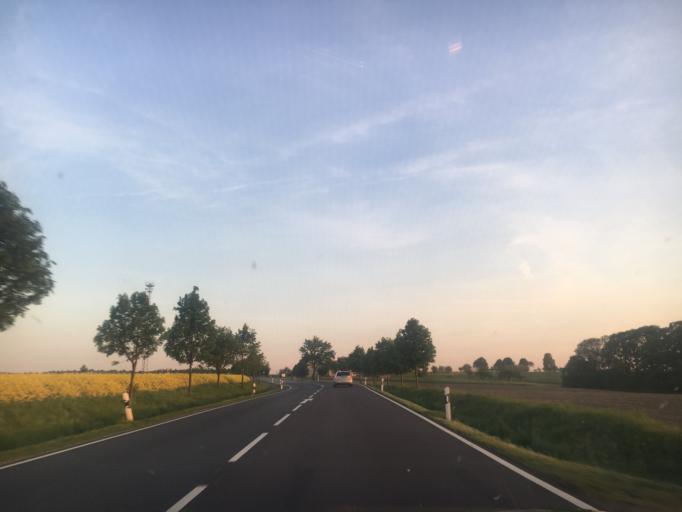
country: DE
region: Thuringia
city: Hirschfeld
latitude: 50.9847
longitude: 12.1371
